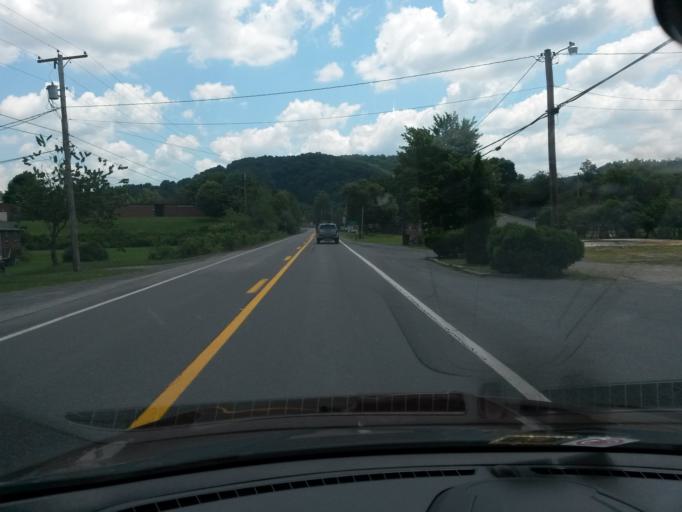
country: US
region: West Virginia
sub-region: Raleigh County
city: Sophia
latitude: 37.7290
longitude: -81.3082
